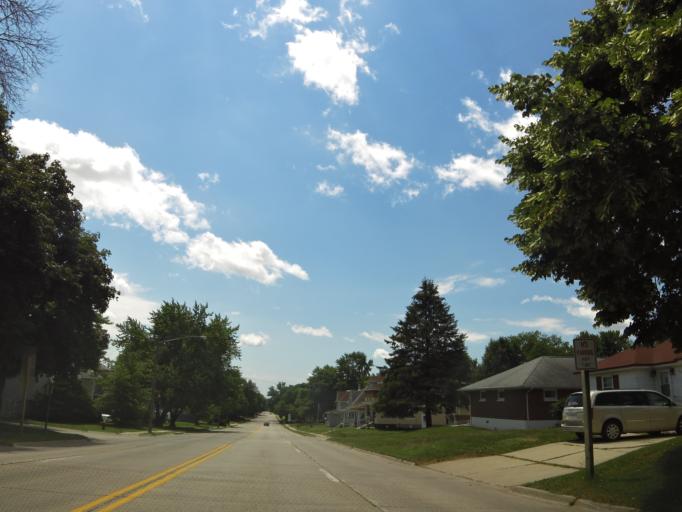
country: US
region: Iowa
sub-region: Fayette County
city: Oelwein
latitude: 42.6874
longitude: -91.9133
